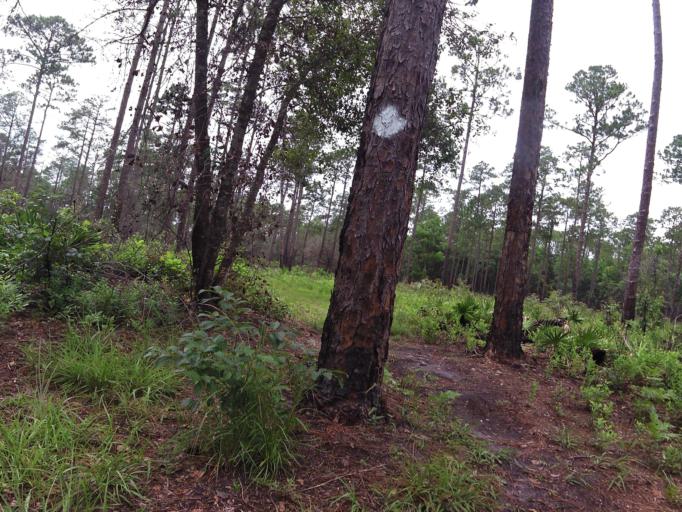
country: US
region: Florida
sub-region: Clay County
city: Green Cove Springs
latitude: 29.9706
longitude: -81.6343
